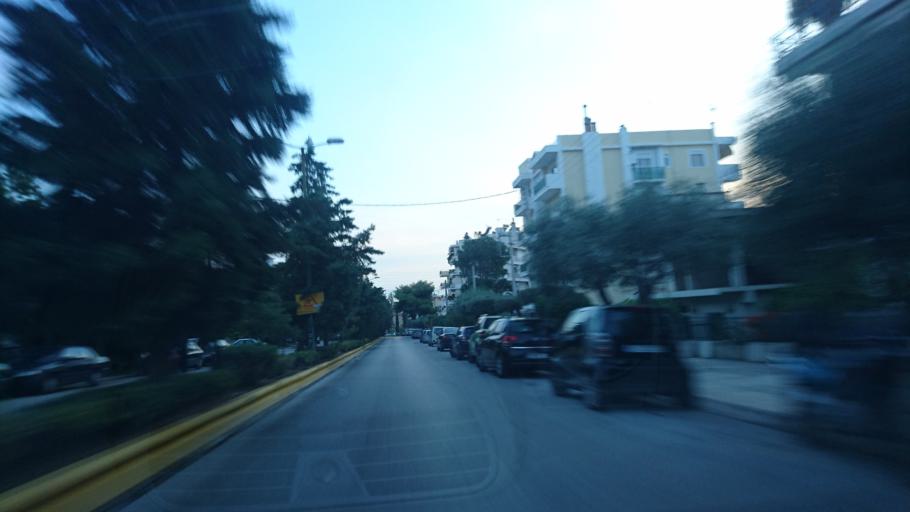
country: GR
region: Attica
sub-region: Nomarchia Athinas
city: Ilioupoli
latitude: 37.9262
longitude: 23.7526
